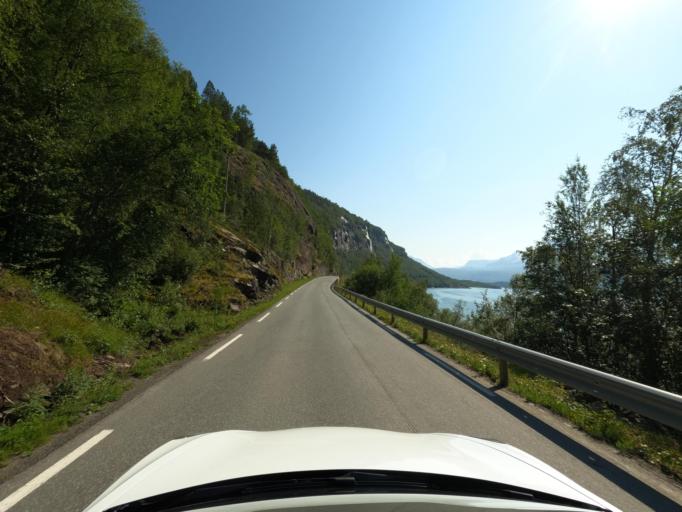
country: NO
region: Nordland
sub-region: Narvik
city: Narvik
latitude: 68.3542
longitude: 17.2738
